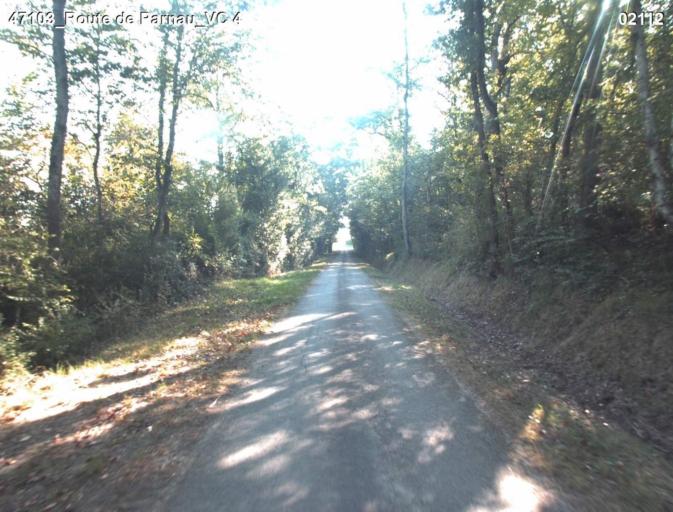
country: FR
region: Aquitaine
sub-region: Departement du Lot-et-Garonne
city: Nerac
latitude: 44.0790
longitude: 0.3537
